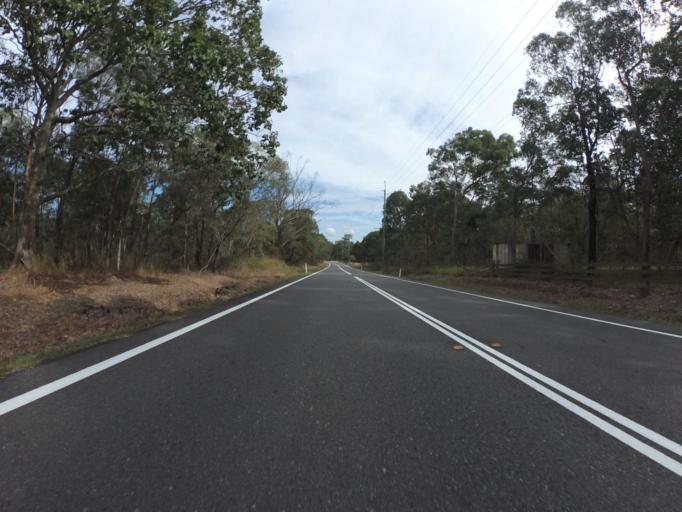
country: AU
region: Queensland
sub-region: Brisbane
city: Moggill
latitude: -27.5759
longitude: 152.8657
